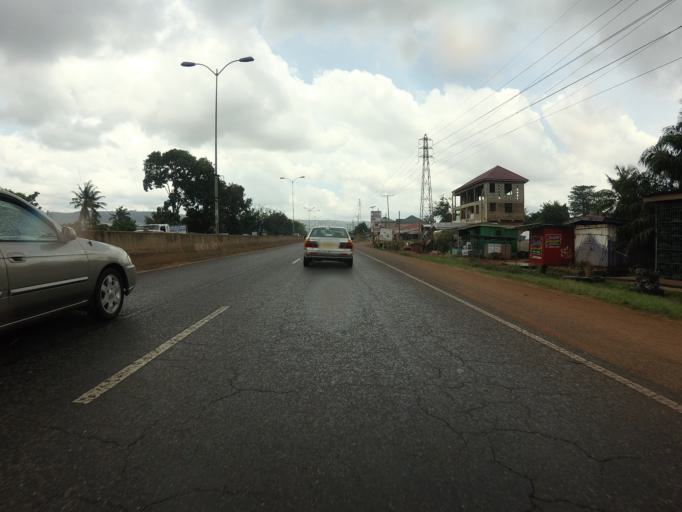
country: GH
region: Greater Accra
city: Medina Estates
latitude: 5.7481
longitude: -0.1775
